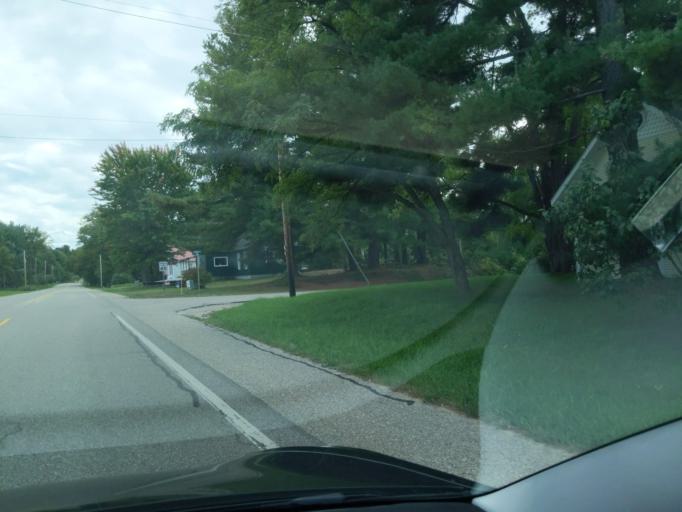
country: US
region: Michigan
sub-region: Kalkaska County
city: Rapid City
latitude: 44.8888
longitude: -85.2723
